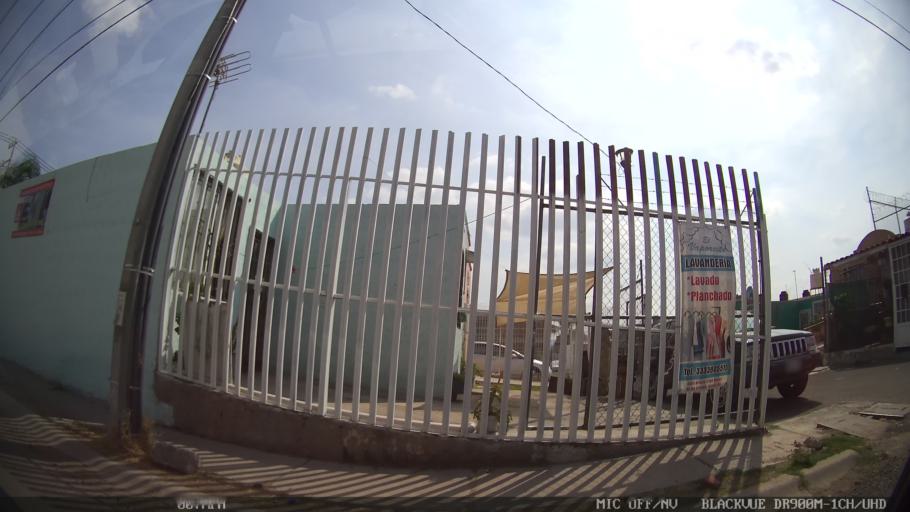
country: MX
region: Jalisco
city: Coyula
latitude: 20.6544
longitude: -103.2115
